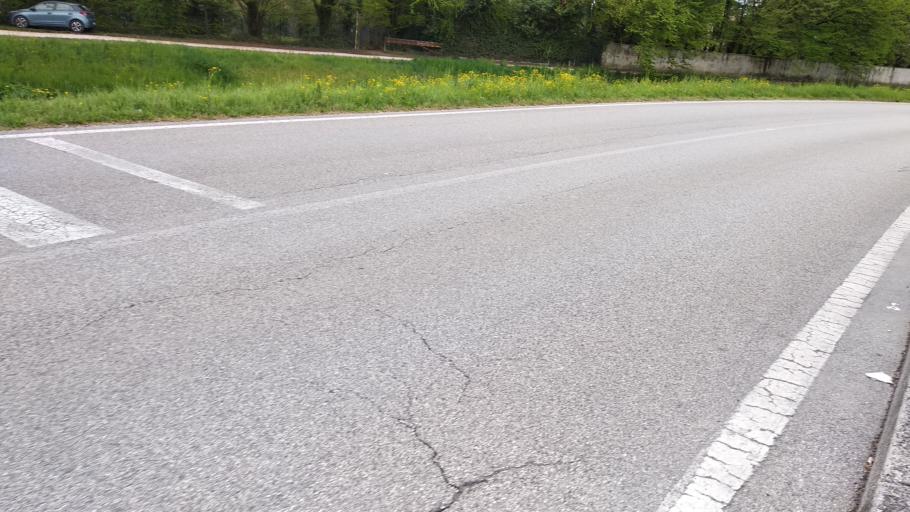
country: IT
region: Veneto
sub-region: Provincia di Venezia
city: Mira Taglio
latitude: 45.4392
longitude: 12.1440
